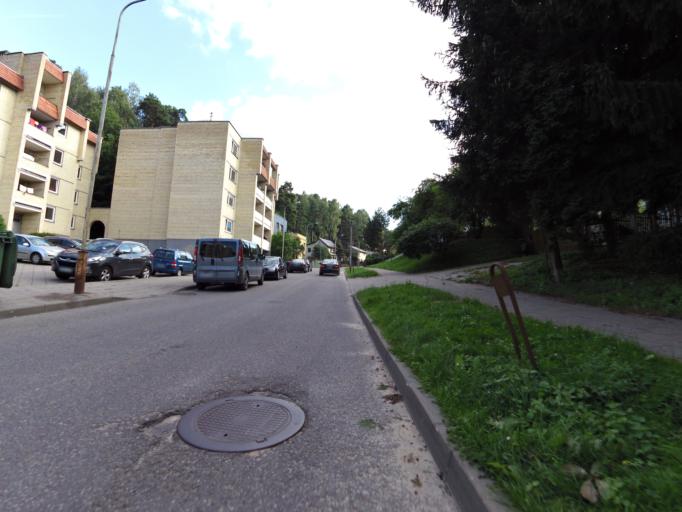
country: LT
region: Vilnius County
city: Rasos
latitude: 54.6938
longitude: 25.3156
